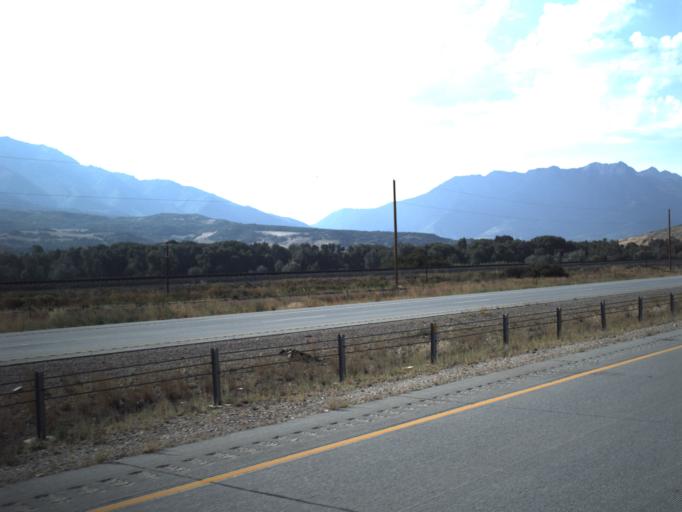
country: US
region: Utah
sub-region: Morgan County
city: Mountain Green
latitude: 41.1040
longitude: -111.7457
